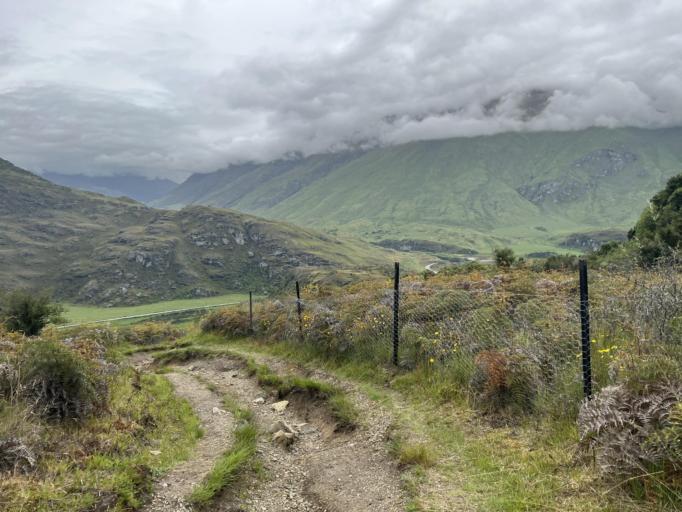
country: NZ
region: Otago
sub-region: Queenstown-Lakes District
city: Wanaka
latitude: -44.6448
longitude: 168.9687
